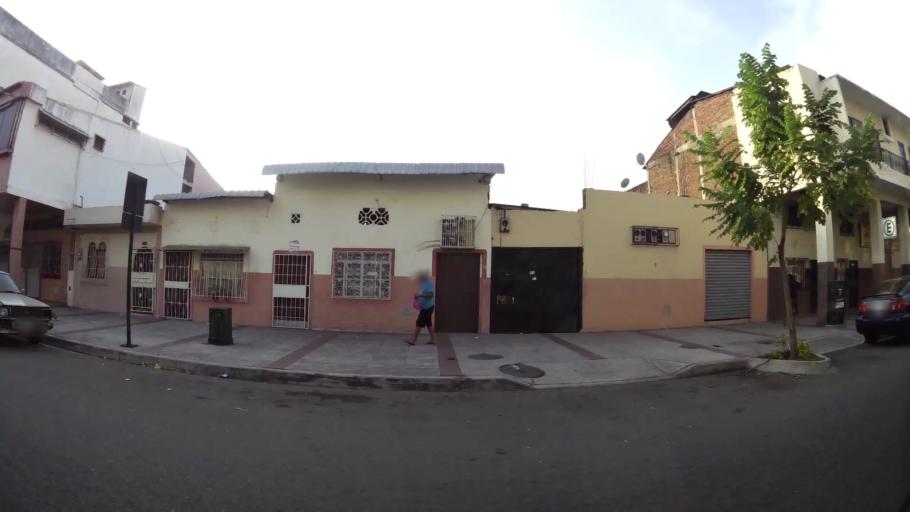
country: EC
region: Guayas
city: Guayaquil
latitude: -2.2036
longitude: -79.8989
